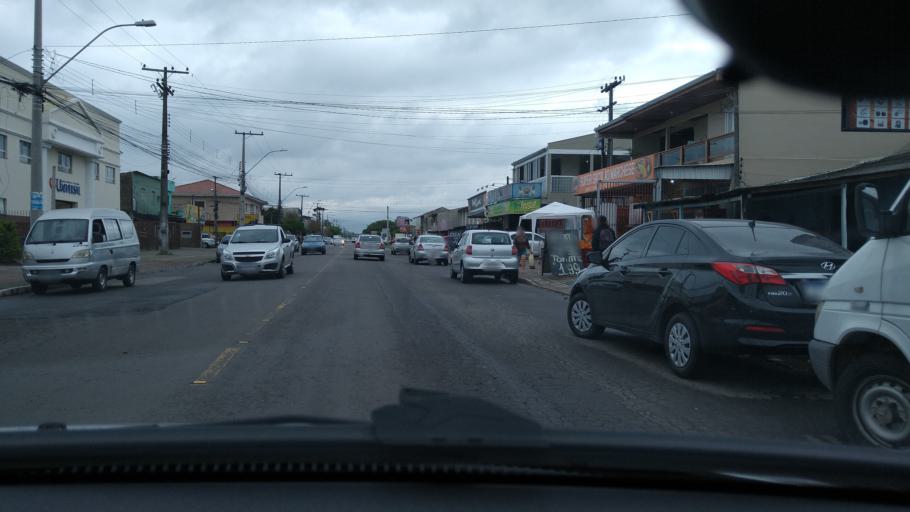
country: BR
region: Rio Grande do Sul
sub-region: Canoas
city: Canoas
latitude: -29.9015
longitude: -51.2140
